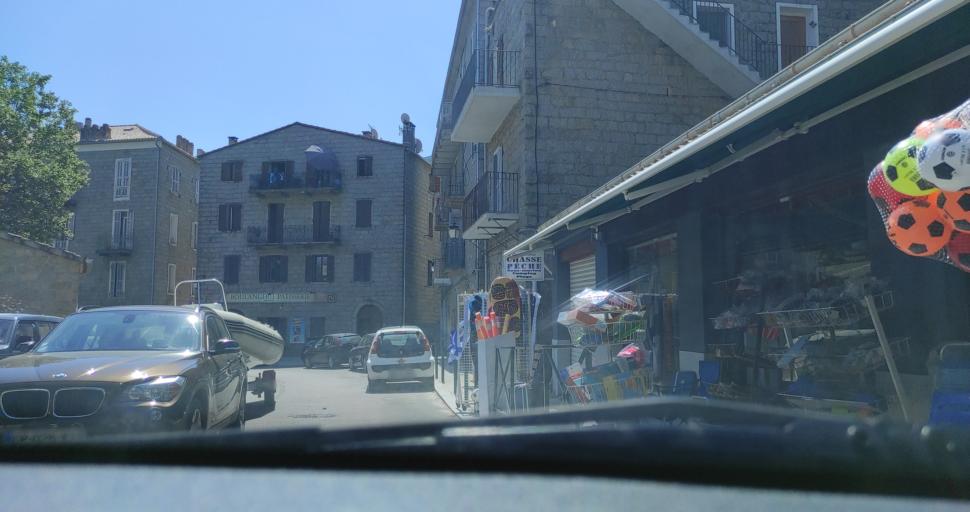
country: FR
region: Corsica
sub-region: Departement de la Corse-du-Sud
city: Sartene
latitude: 41.6180
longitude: 8.9726
